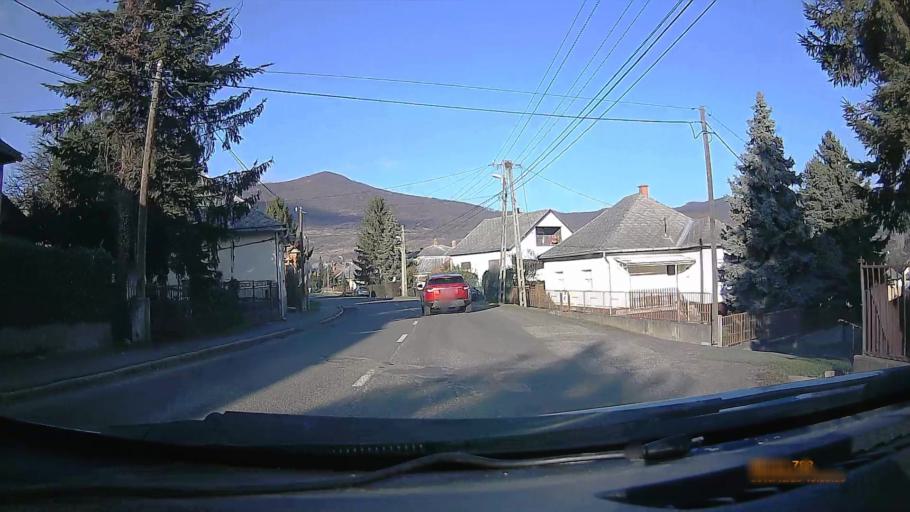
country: HU
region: Heves
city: Abasar
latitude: 47.8234
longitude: 20.0538
